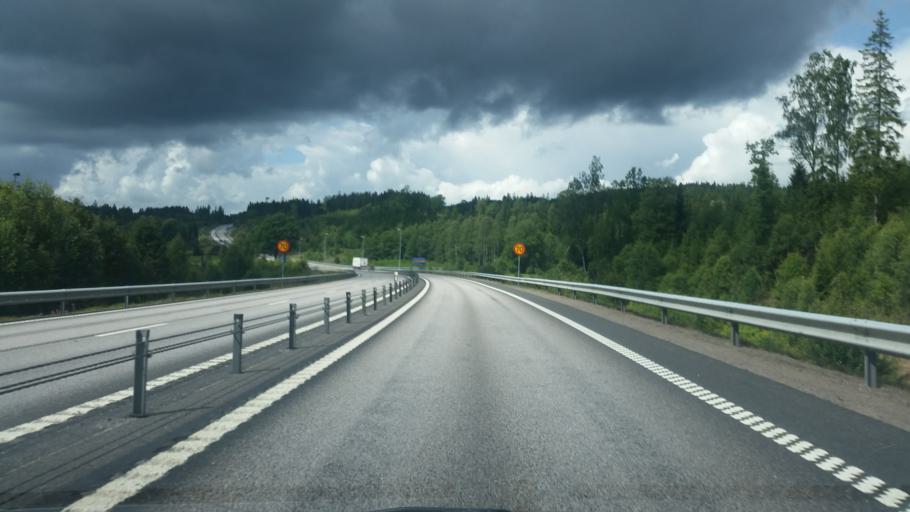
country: SE
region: Vaestra Goetaland
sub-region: Boras Kommun
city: Ganghester
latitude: 57.6703
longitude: 13.0253
